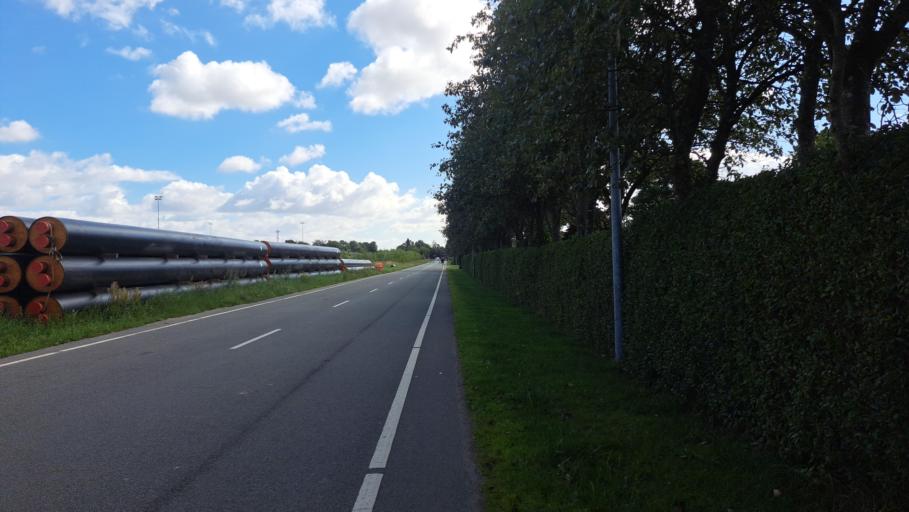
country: DK
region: Central Jutland
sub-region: Hedensted Kommune
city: Hedensted
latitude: 55.7786
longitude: 9.6852
